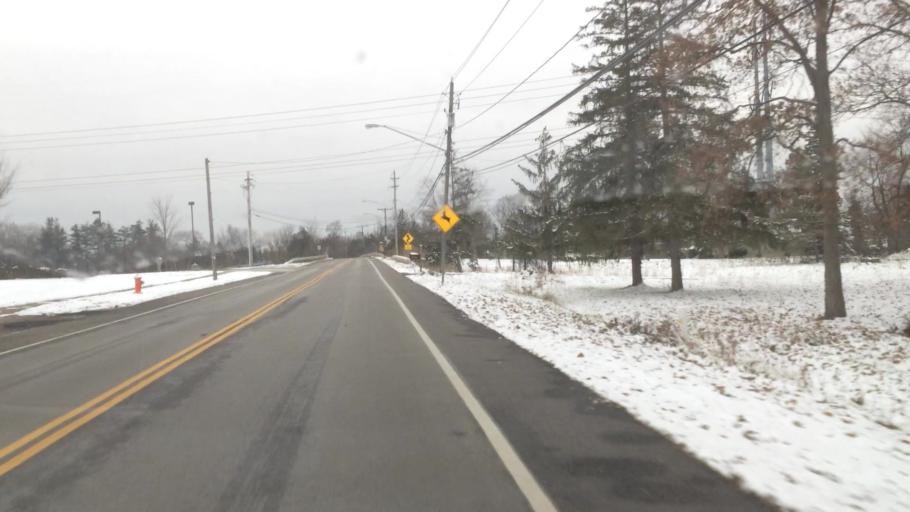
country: US
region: Ohio
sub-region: Cuyahoga County
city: Middleburg Heights
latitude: 41.3306
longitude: -81.8010
